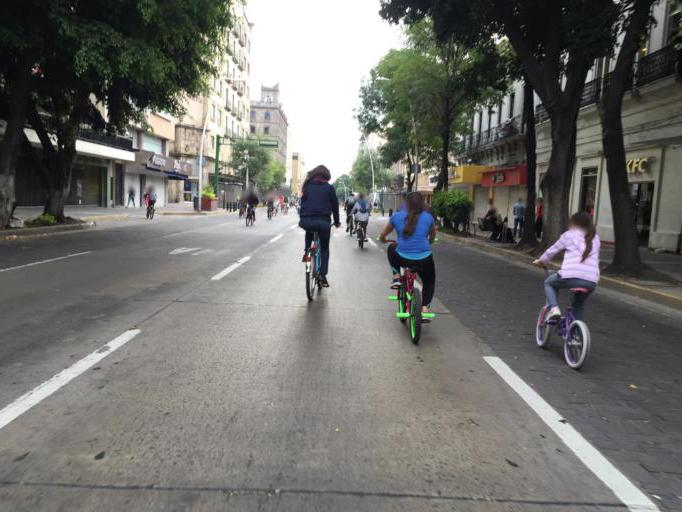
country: MX
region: Jalisco
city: Guadalajara
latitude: 20.6751
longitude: -103.3494
